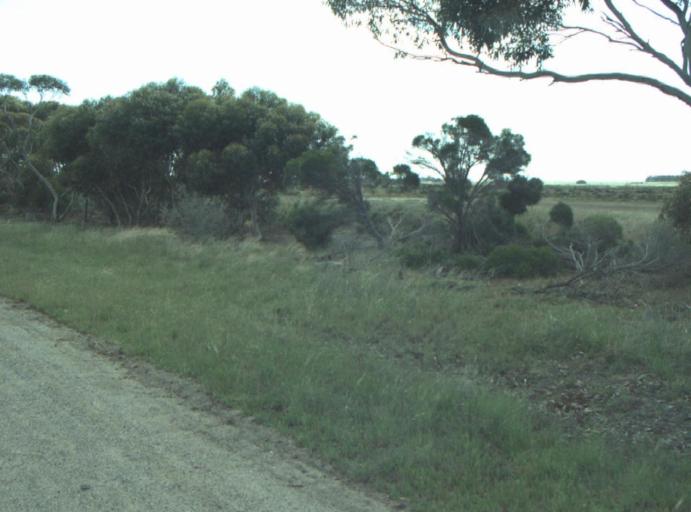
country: AU
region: Victoria
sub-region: Greater Geelong
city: Lara
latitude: -38.0655
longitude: 144.4258
